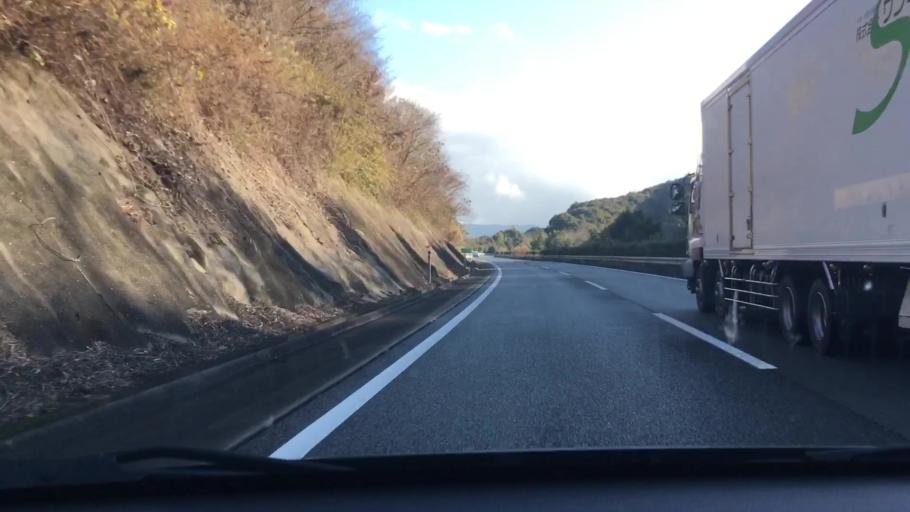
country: JP
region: Kumamoto
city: Hitoyoshi
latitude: 32.1720
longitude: 130.7908
